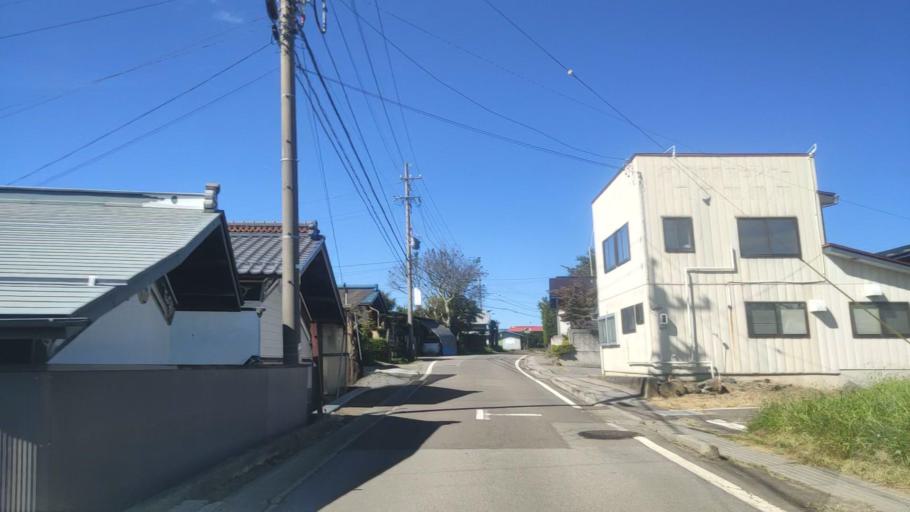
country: JP
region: Nagano
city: Chino
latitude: 35.9684
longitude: 138.2183
